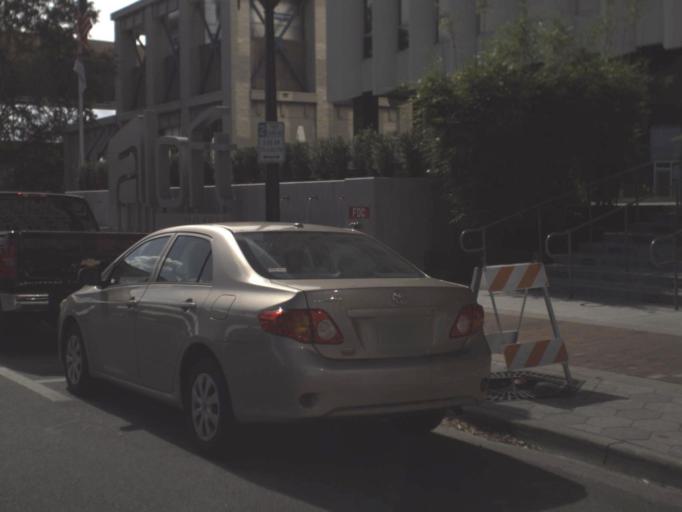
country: US
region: Florida
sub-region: Orange County
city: Orlando
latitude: 28.5366
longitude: -81.3787
